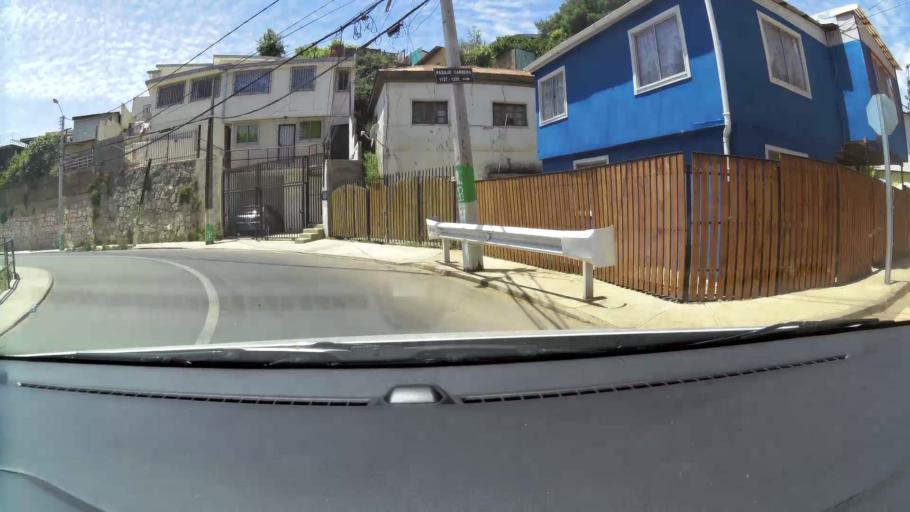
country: CL
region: Valparaiso
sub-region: Provincia de Valparaiso
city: Vina del Mar
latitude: -33.0440
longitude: -71.5869
